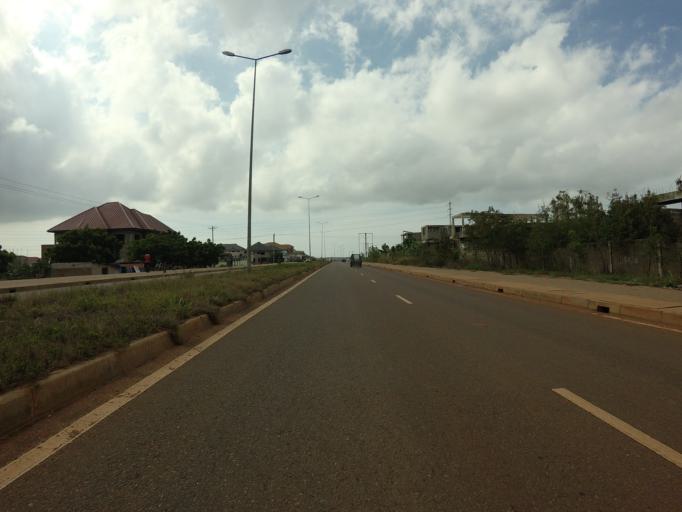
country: GH
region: Greater Accra
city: Teshi Old Town
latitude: 5.6033
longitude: -0.1380
